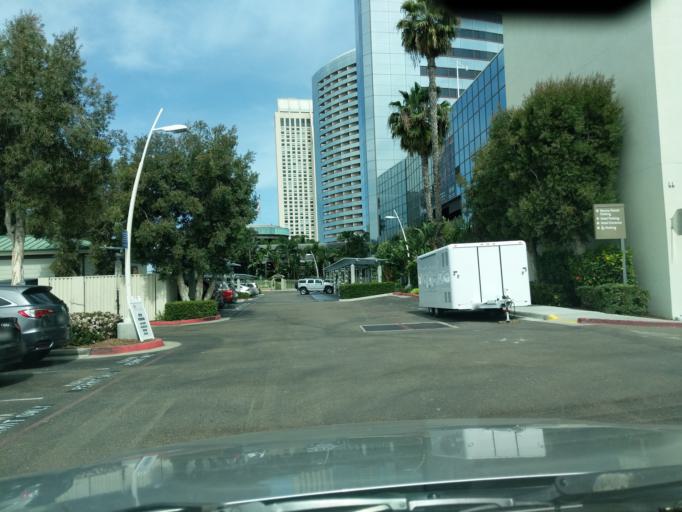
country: US
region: California
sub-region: San Diego County
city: San Diego
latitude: 32.7069
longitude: -117.1645
